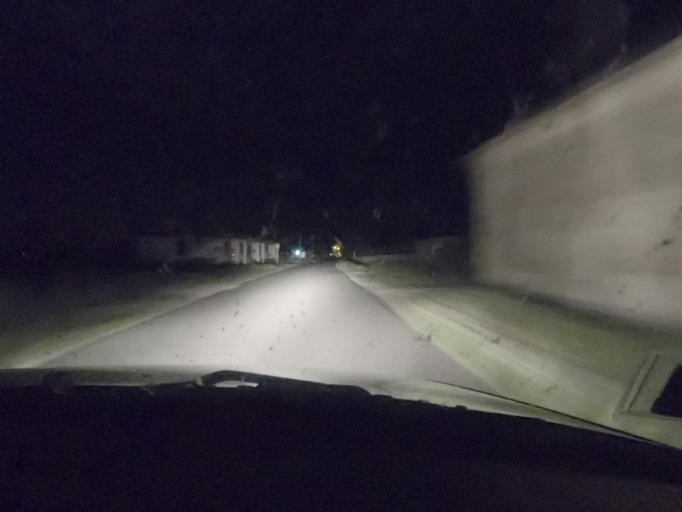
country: ES
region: Castille and Leon
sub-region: Provincia de Salamanca
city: Ciudad Rodrigo
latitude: 40.5861
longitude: -6.5418
